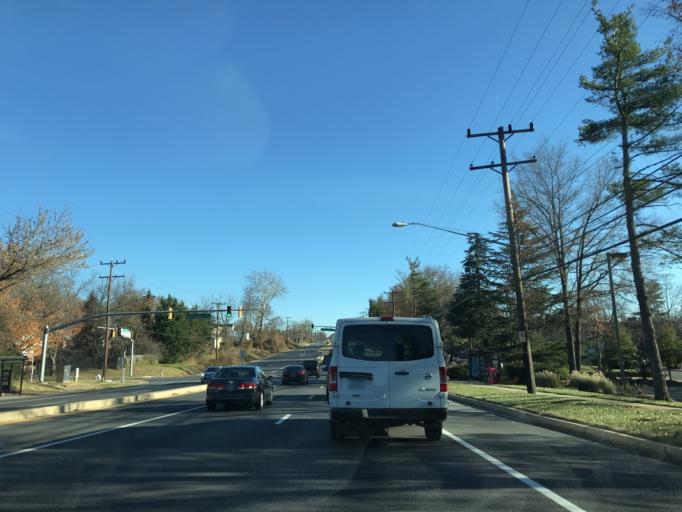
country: US
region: Maryland
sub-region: Montgomery County
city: Aspen Hill
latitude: 39.0635
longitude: -77.0955
